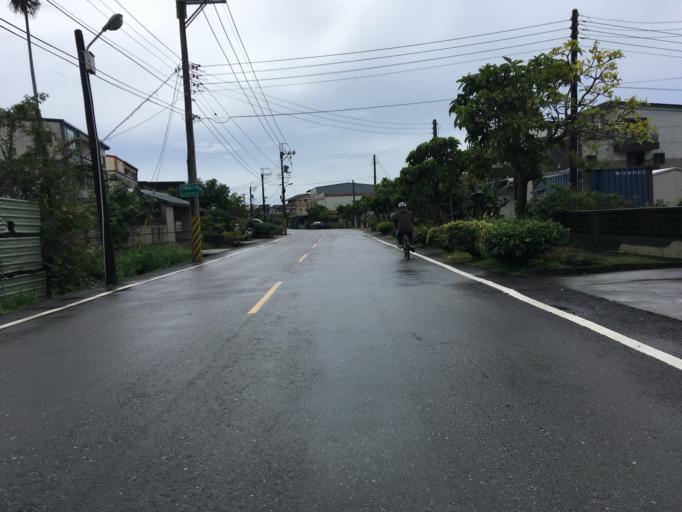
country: TW
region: Taiwan
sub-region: Yilan
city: Yilan
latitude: 24.6683
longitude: 121.7879
